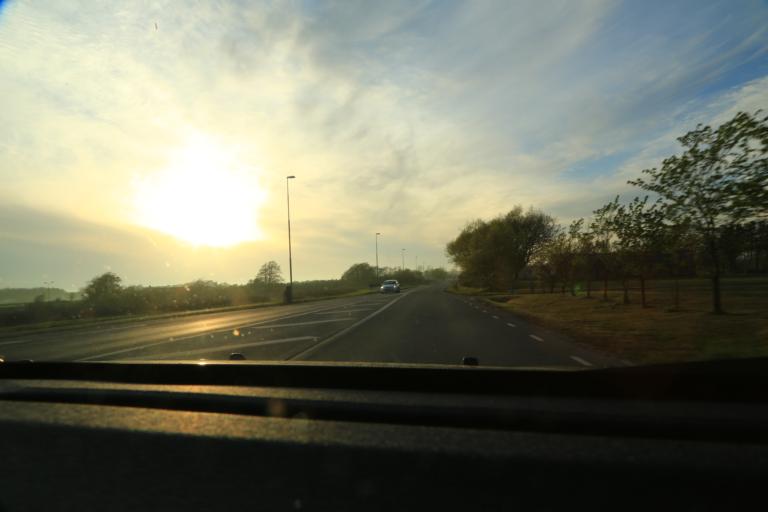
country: SE
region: Halland
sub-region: Varbergs Kommun
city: Traslovslage
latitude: 57.0738
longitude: 12.2860
